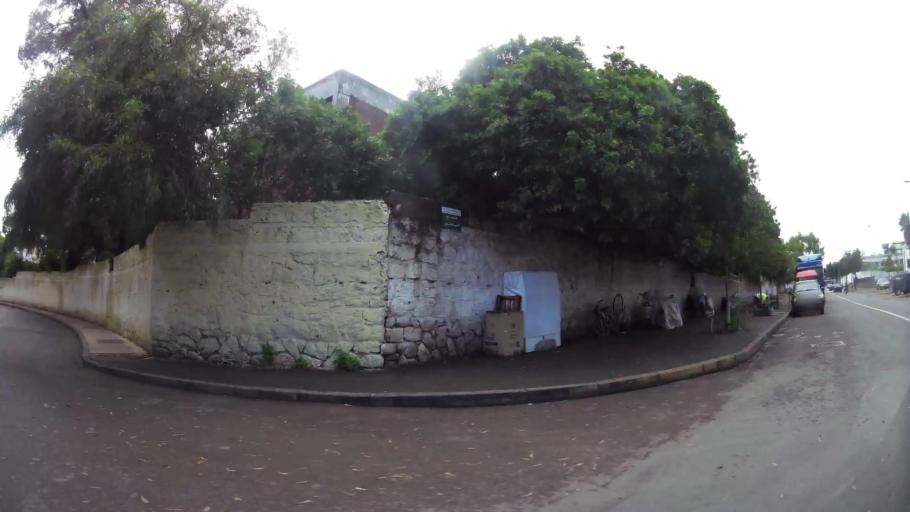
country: MA
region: Grand Casablanca
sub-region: Casablanca
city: Casablanca
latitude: 33.5643
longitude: -7.6117
